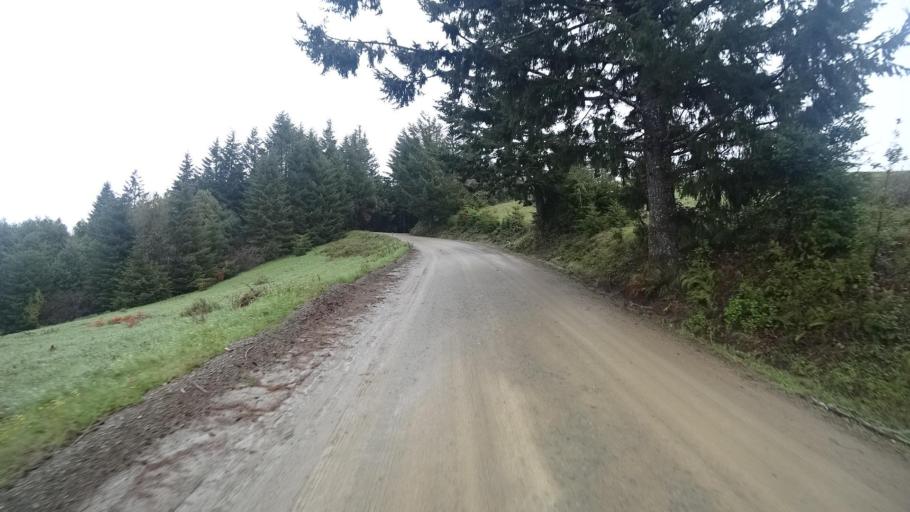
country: US
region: California
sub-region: Humboldt County
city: Westhaven-Moonstone
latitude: 41.1411
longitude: -123.8620
